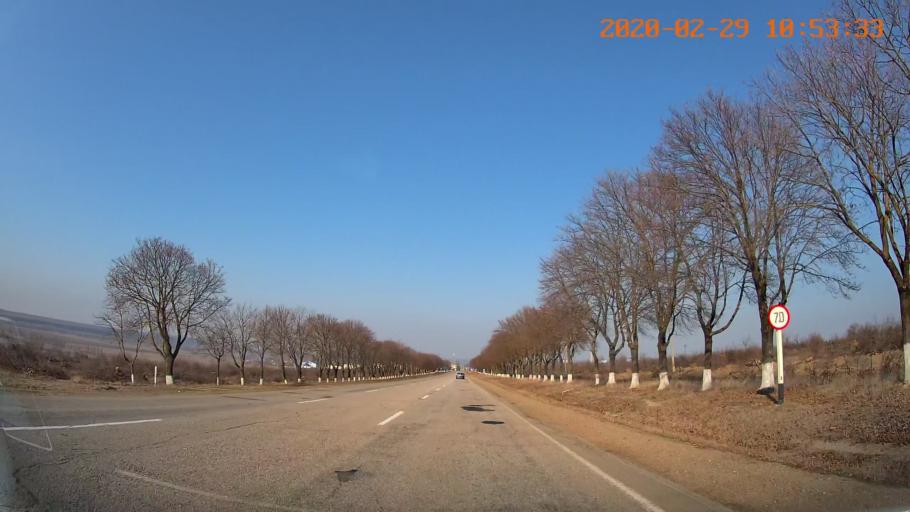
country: MD
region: Telenesti
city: Grigoriopol
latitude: 47.1168
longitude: 29.3340
